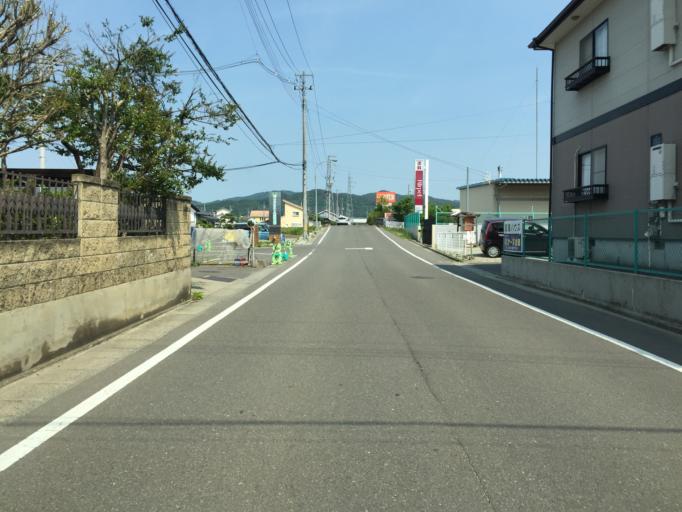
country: JP
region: Fukushima
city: Fukushima-shi
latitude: 37.7358
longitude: 140.4526
